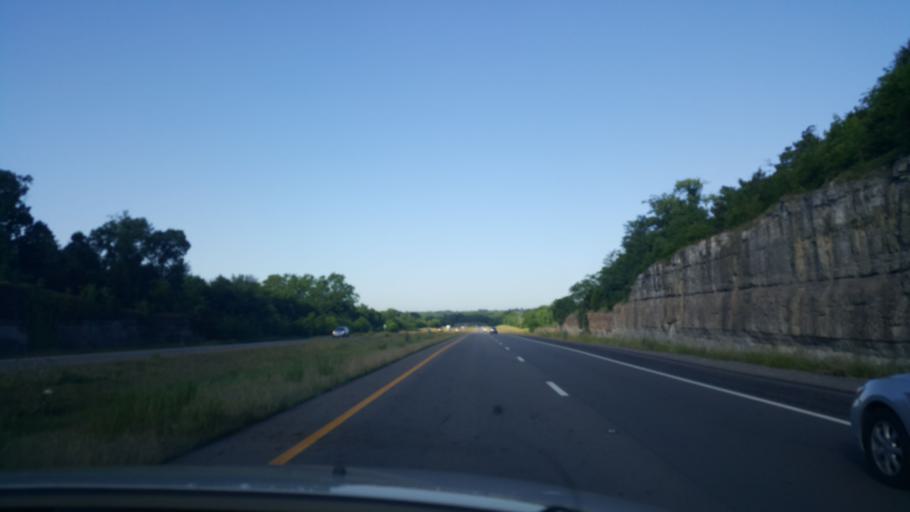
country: US
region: Tennessee
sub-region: Maury County
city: Columbia
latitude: 35.6270
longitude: -87.1080
